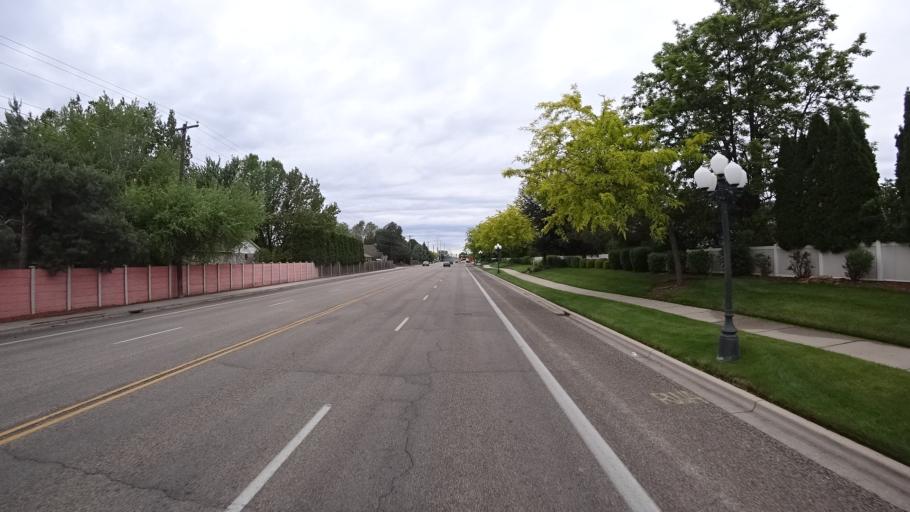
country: US
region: Idaho
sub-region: Ada County
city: Eagle
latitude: 43.6485
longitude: -116.3300
